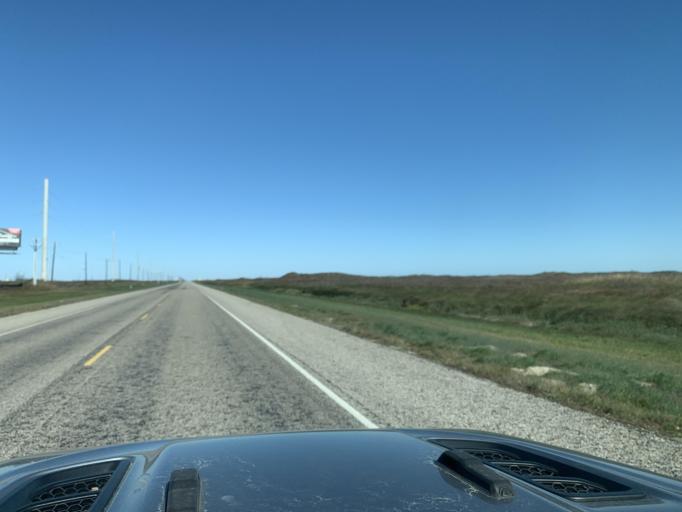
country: US
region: Texas
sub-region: Nueces County
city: Port Aransas
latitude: 27.6427
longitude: -97.1969
